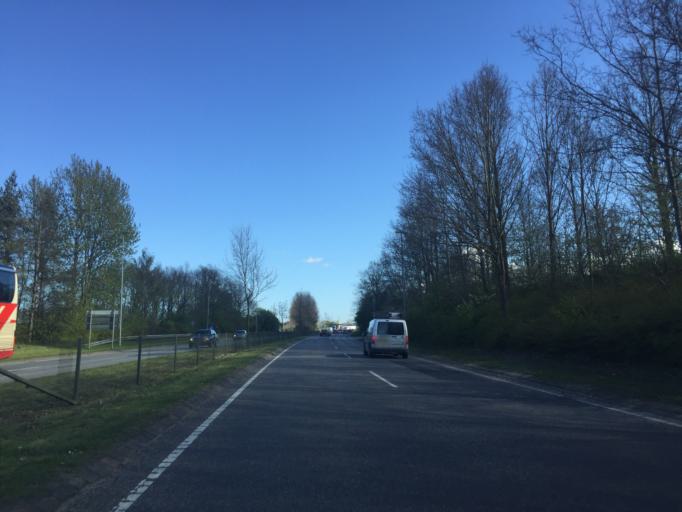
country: DK
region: South Denmark
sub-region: Odense Kommune
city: Neder Holluf
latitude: 55.3668
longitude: 10.4549
